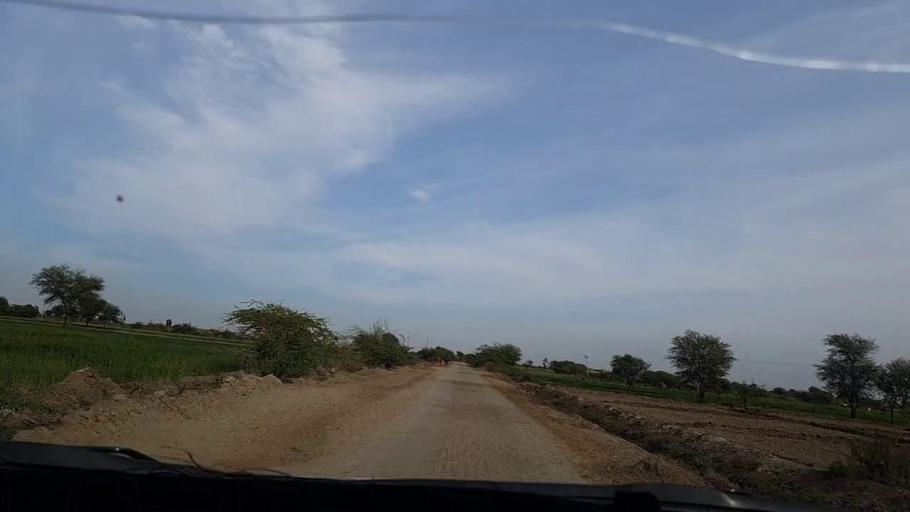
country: PK
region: Sindh
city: Dhoro Naro
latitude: 25.4752
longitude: 69.5324
